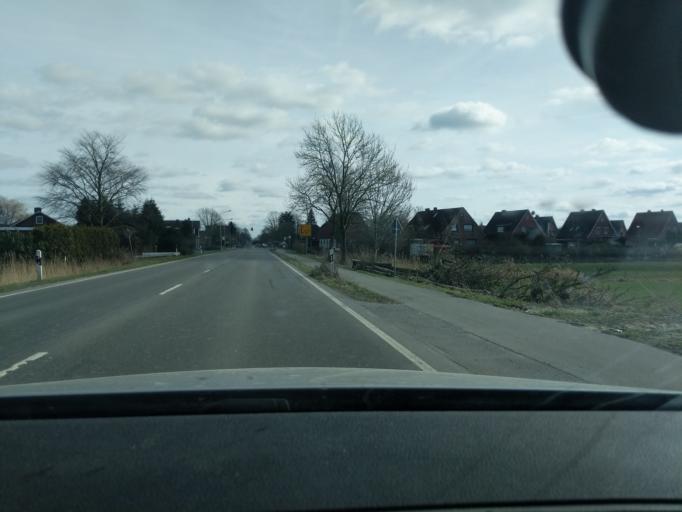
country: DE
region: Lower Saxony
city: Drochtersen
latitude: 53.7007
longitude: 9.4088
